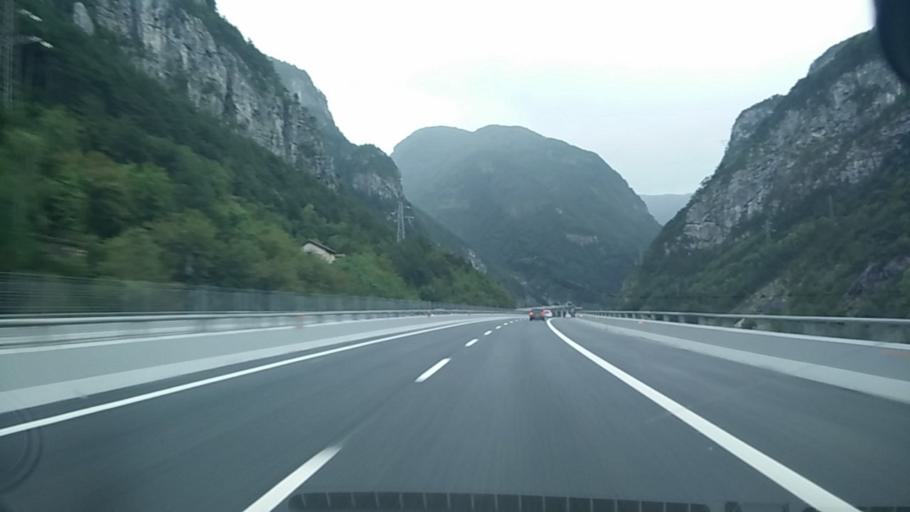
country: IT
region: Friuli Venezia Giulia
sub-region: Provincia di Udine
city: Dogna
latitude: 46.4319
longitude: 13.3148
